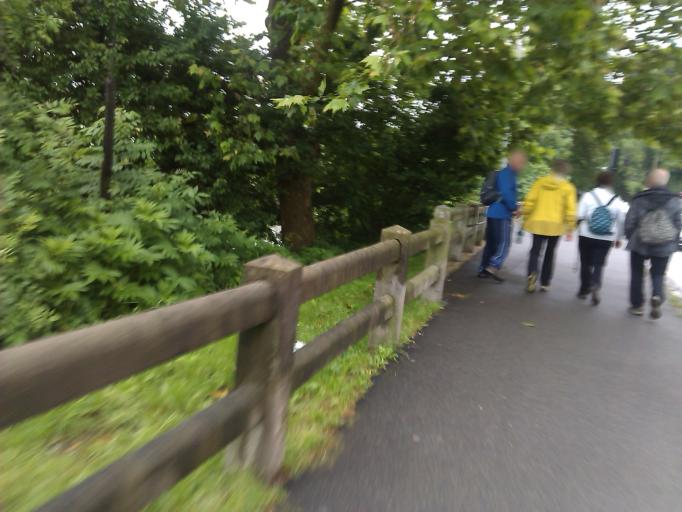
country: ES
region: Basque Country
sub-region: Provincia de Guipuzcoa
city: San Sebastian
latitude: 43.3072
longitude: -1.9661
